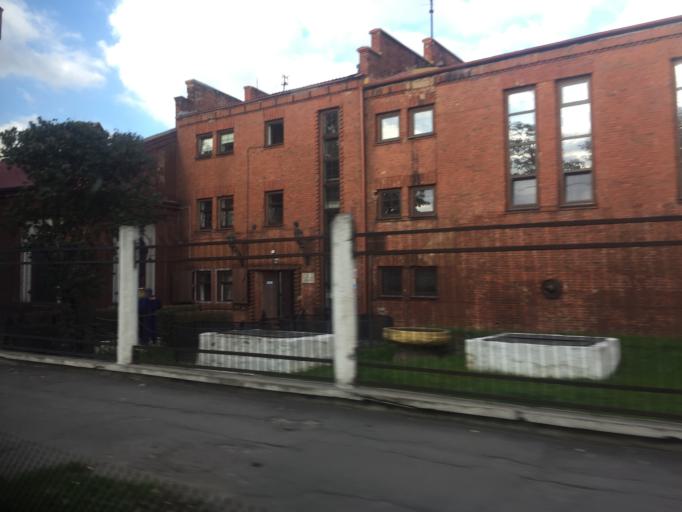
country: RU
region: Kaliningrad
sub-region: Gorod Kaliningrad
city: Kaliningrad
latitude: 54.7386
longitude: 20.4792
